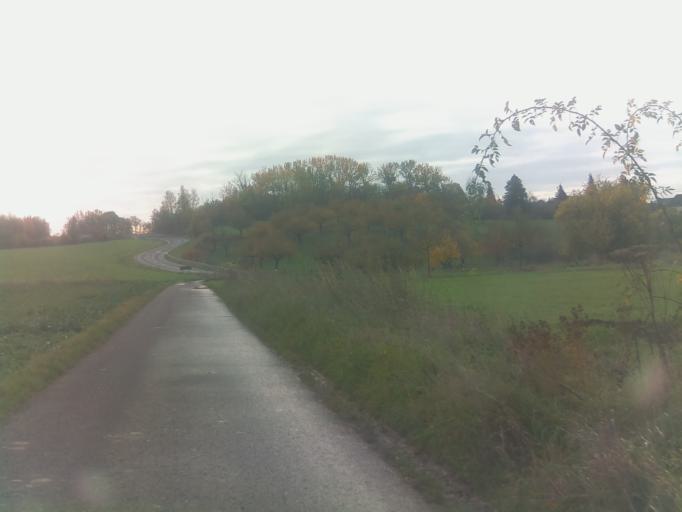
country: DE
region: Hesse
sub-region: Regierungsbezirk Darmstadt
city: Altenstadt
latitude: 50.3077
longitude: 8.9548
